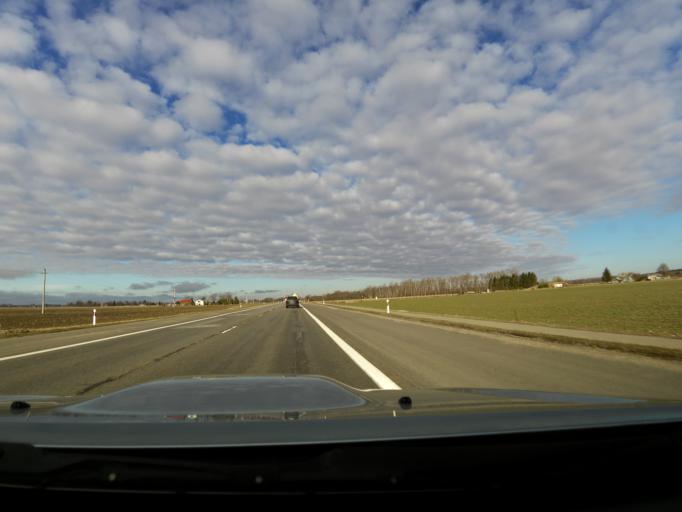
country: LT
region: Panevezys
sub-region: Panevezys City
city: Panevezys
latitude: 55.7394
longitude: 24.1937
